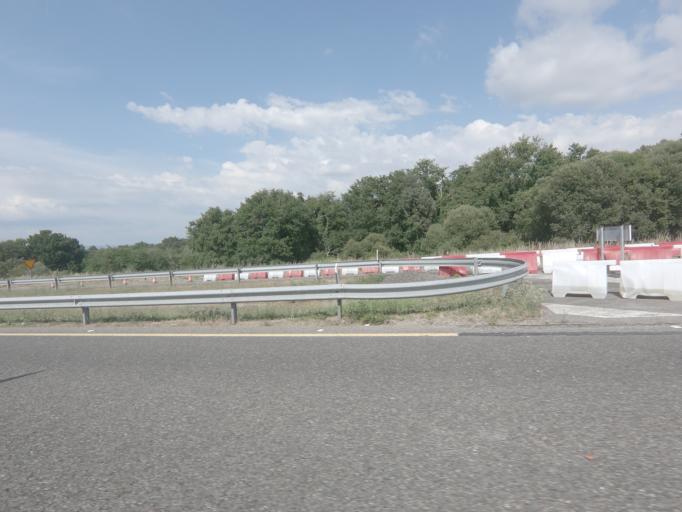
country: ES
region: Galicia
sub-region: Provincia de Ourense
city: Taboadela
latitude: 42.2535
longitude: -7.8683
